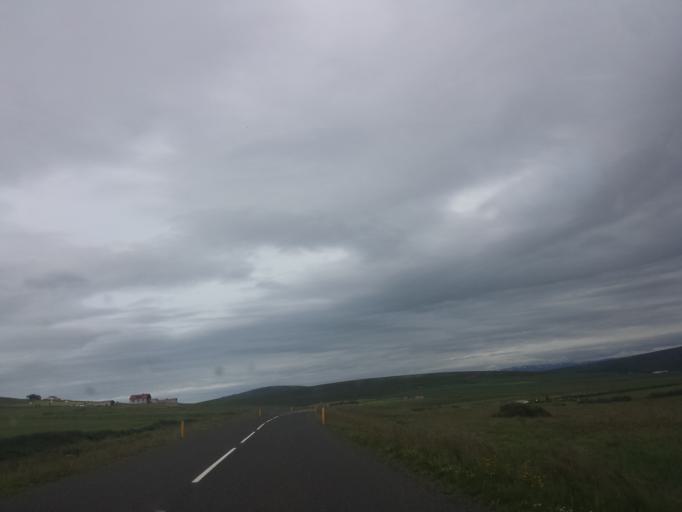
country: IS
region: Northeast
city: Laugar
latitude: 65.7086
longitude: -17.6152
